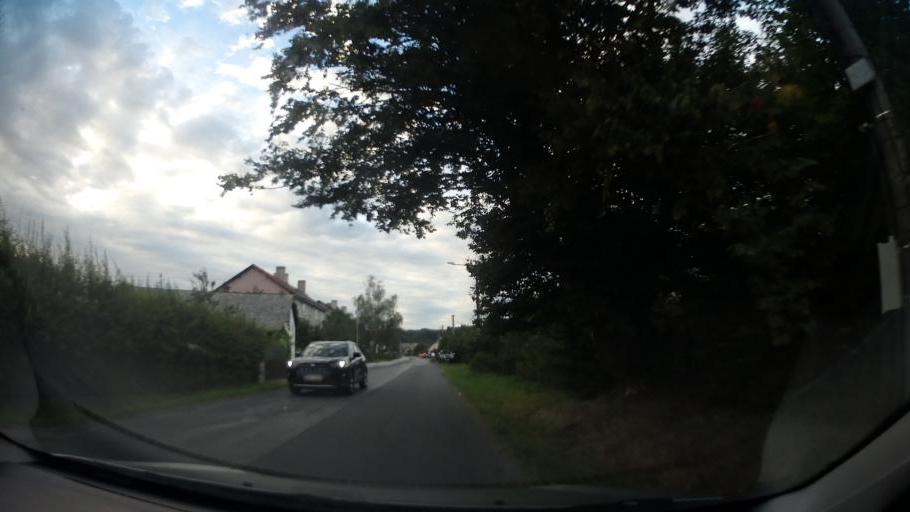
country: CZ
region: Olomoucky
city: Paseka
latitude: 49.8165
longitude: 17.2027
